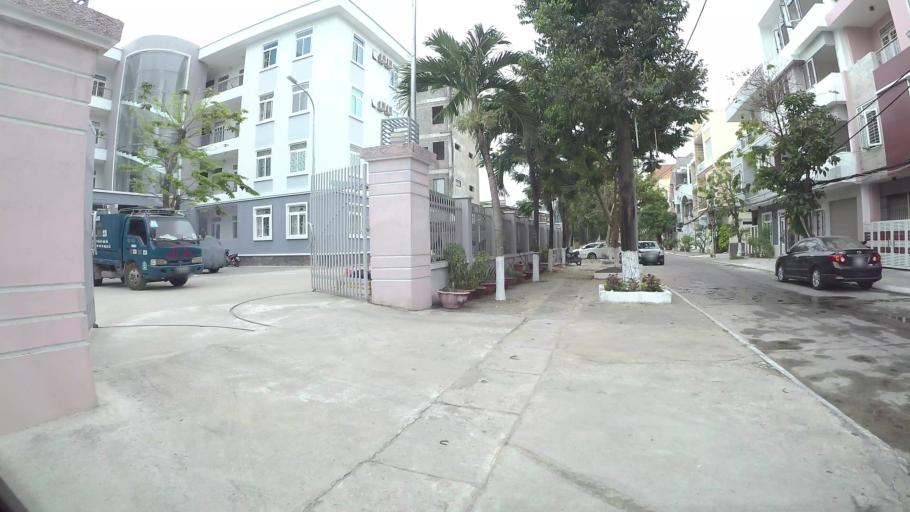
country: VN
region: Da Nang
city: Da Nang
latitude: 16.0513
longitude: 108.2109
